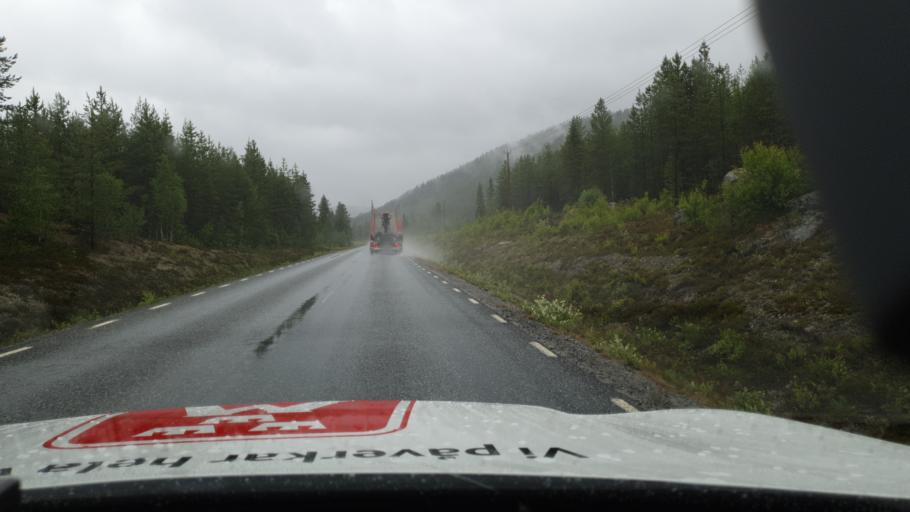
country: SE
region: Vaesterbotten
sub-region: Asele Kommun
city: Asele
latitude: 64.3083
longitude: 17.2403
